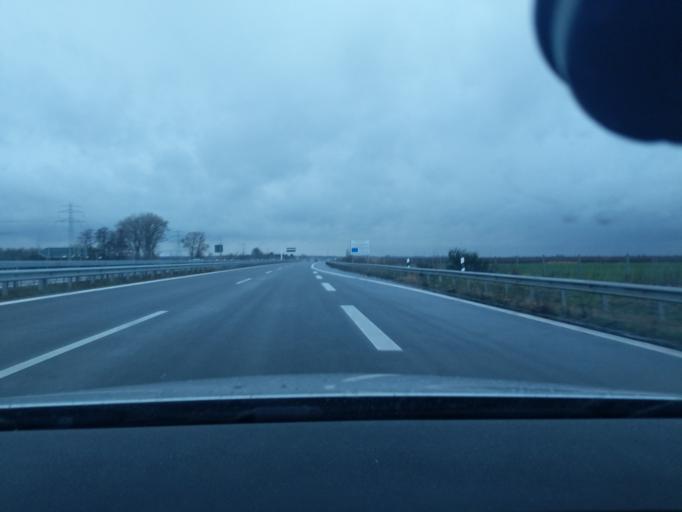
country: DE
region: Lower Saxony
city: Jork
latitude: 53.5012
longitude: 9.6586
